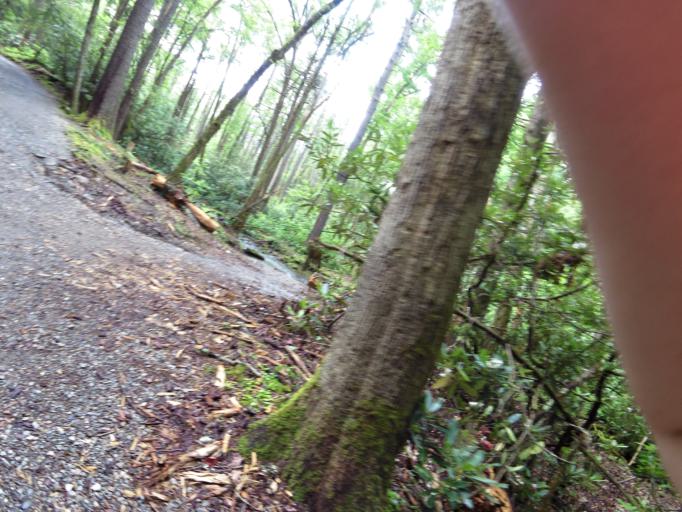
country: US
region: Tennessee
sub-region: Blount County
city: Wildwood
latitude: 35.6036
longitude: -83.7678
